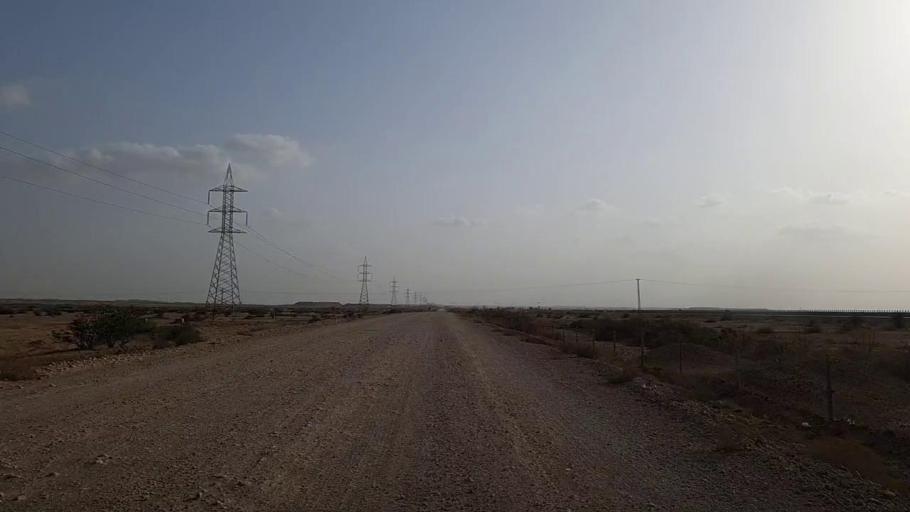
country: PK
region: Sindh
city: Kotri
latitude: 25.2070
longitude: 67.8920
